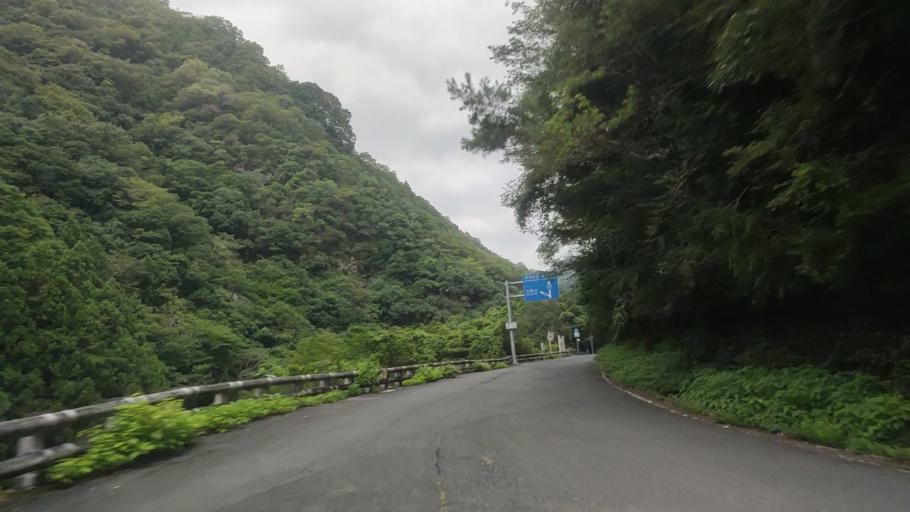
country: JP
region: Wakayama
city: Hashimoto
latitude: 34.2715
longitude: 135.6356
